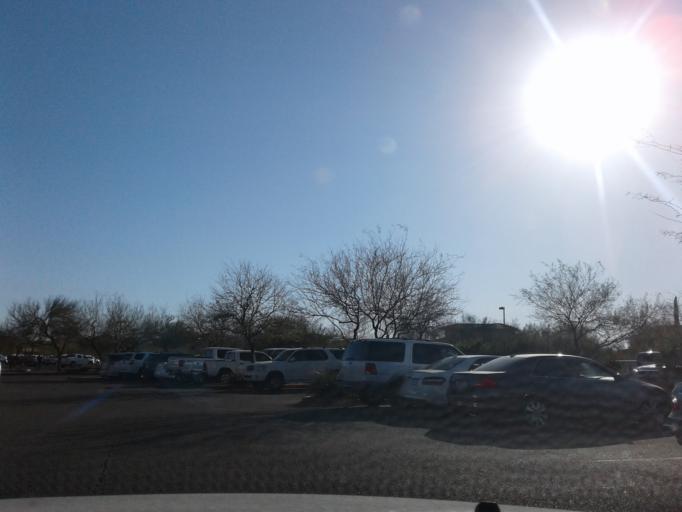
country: US
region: Arizona
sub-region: Maricopa County
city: Paradise Valley
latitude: 33.6694
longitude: -111.9097
